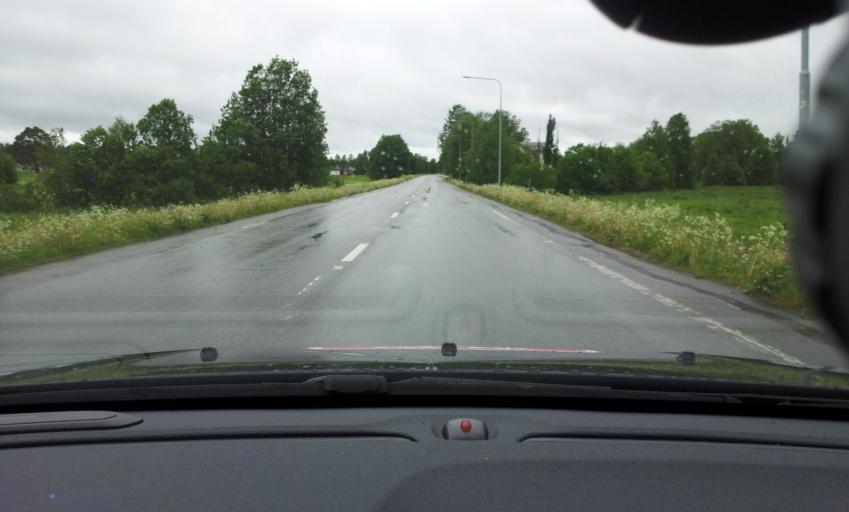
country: SE
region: Jaemtland
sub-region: Krokoms Kommun
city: Krokom
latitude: 63.3061
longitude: 14.4675
